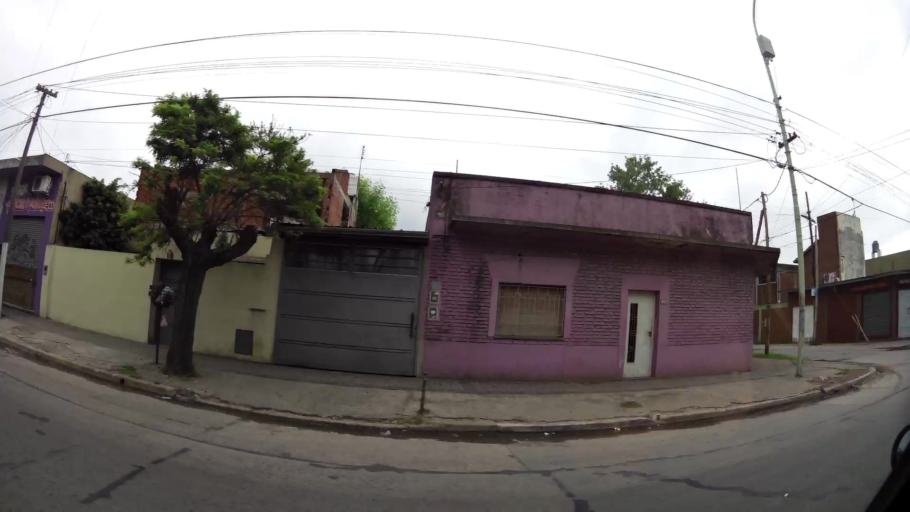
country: AR
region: Buenos Aires
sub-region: Partido de Quilmes
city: Quilmes
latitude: -34.7786
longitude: -58.2411
